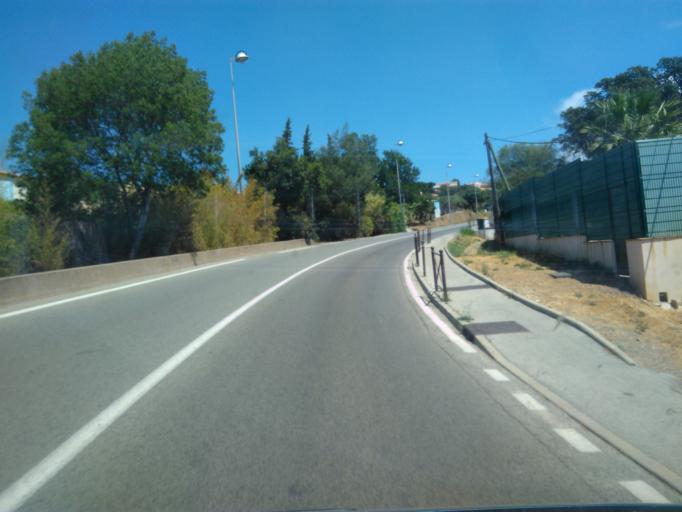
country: FR
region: Provence-Alpes-Cote d'Azur
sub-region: Departement du Var
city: La Croix-Valmer
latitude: 43.2046
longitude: 6.5631
